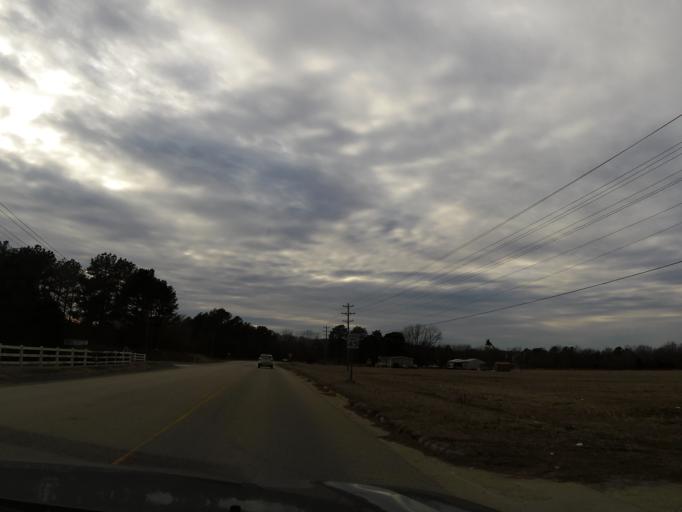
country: US
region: North Carolina
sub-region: Nash County
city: Rocky Mount
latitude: 35.9765
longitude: -77.7449
